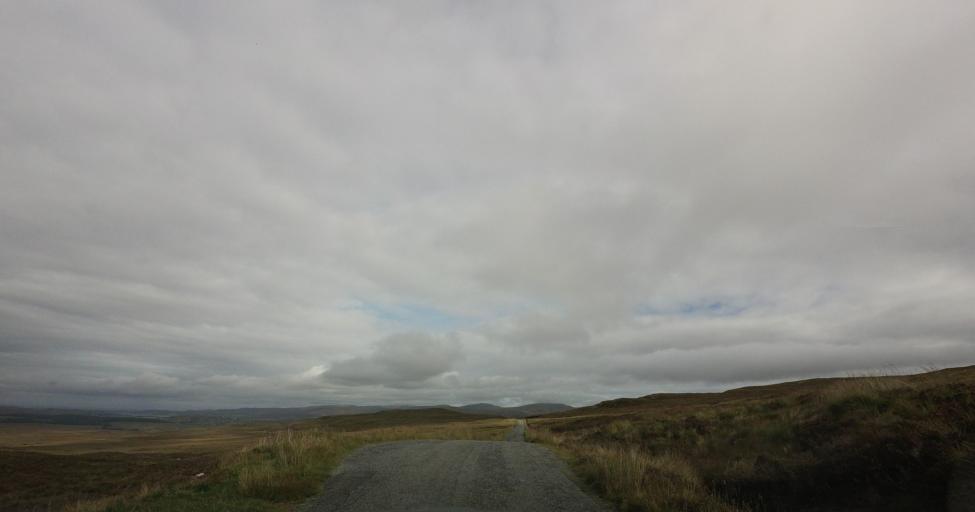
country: GB
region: Scotland
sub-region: Highland
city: Isle of Skye
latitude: 57.4032
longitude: -6.2680
